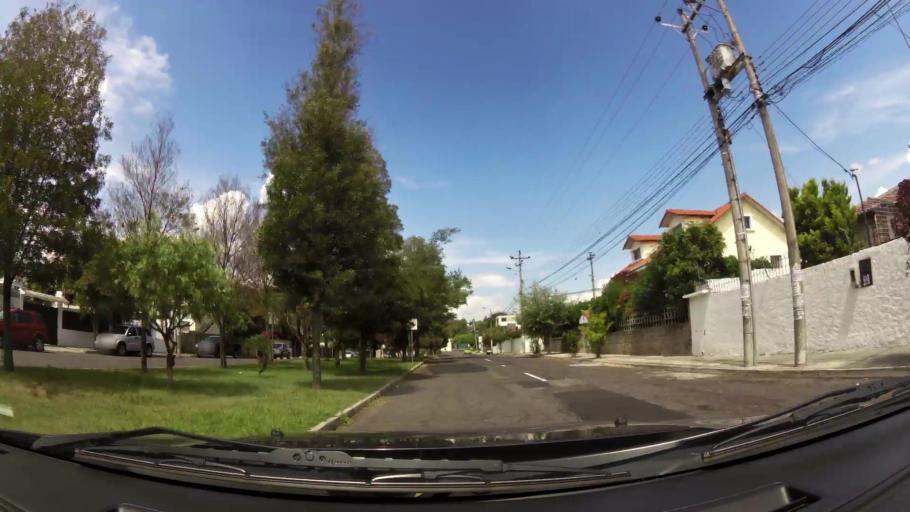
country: EC
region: Pichincha
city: Quito
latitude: -0.2125
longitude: -78.4294
